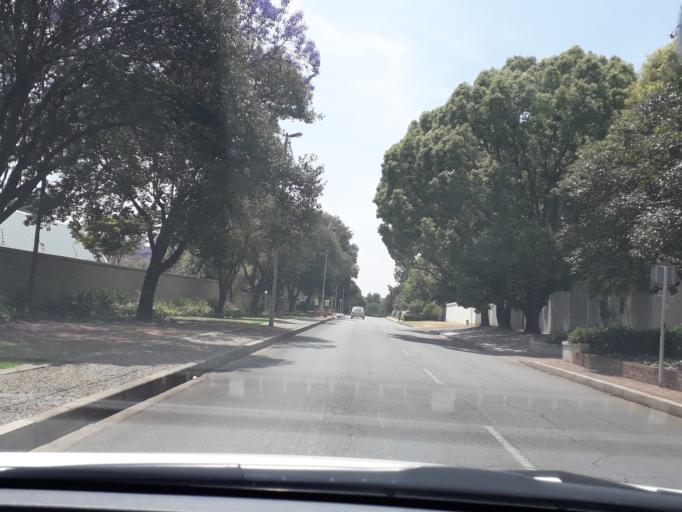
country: ZA
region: Gauteng
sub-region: City of Johannesburg Metropolitan Municipality
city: Johannesburg
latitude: -26.1077
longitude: 28.0267
